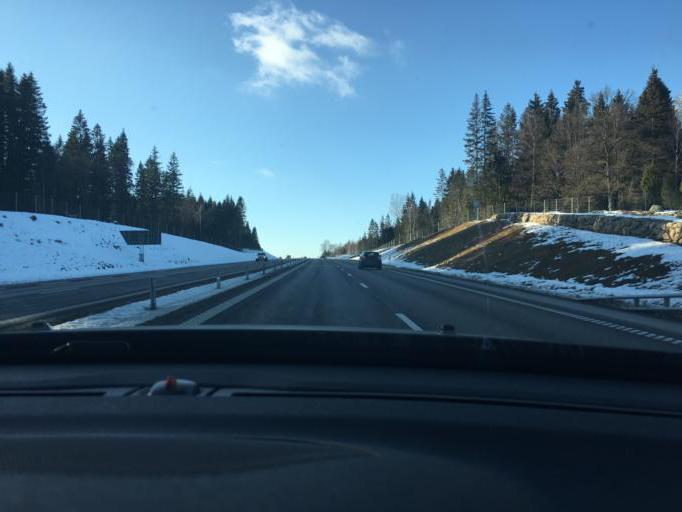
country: SE
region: Vaestra Goetaland
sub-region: Ulricehamns Kommun
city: Ulricehamn
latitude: 57.8195
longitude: 13.3356
